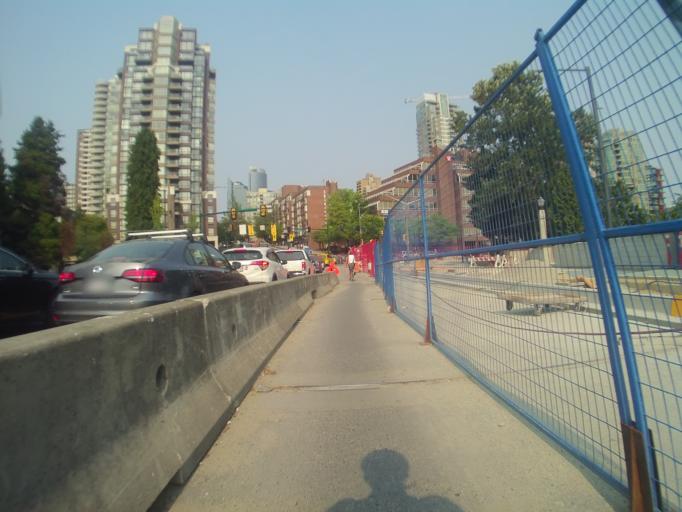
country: CA
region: British Columbia
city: West End
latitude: 49.2763
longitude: -123.1331
